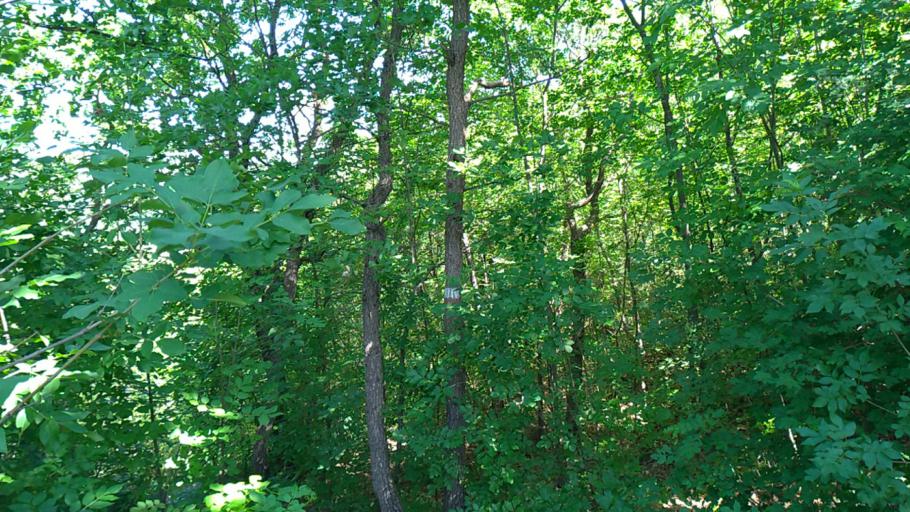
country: IT
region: Emilia-Romagna
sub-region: Provincia di Modena
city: Guiglia
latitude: 44.4114
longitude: 10.9285
